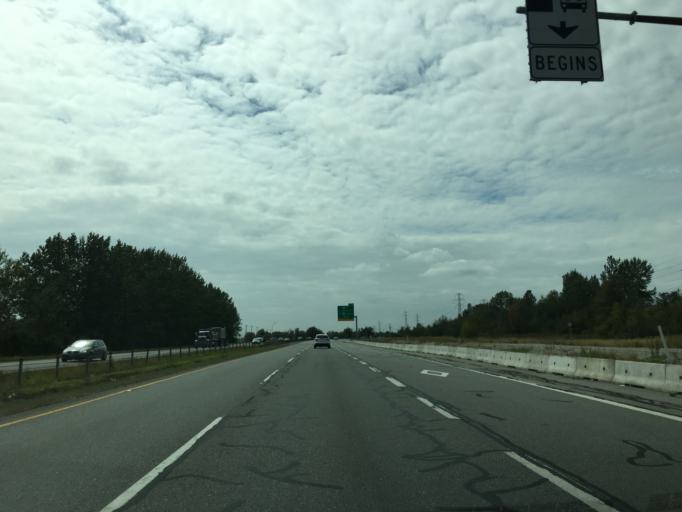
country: CA
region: British Columbia
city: Ladner
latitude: 49.0905
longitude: -122.9970
